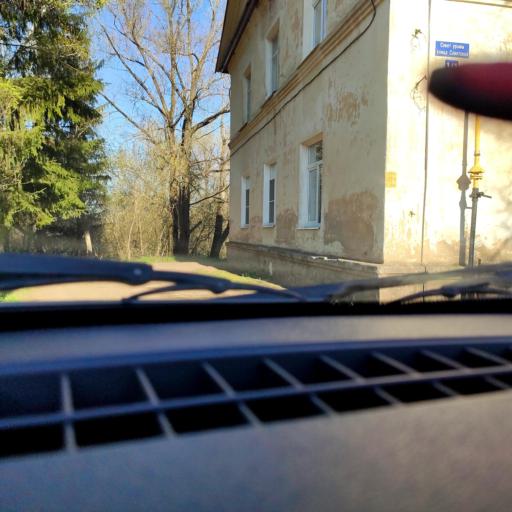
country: RU
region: Bashkortostan
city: Mikhaylovka
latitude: 54.7755
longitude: 55.8381
